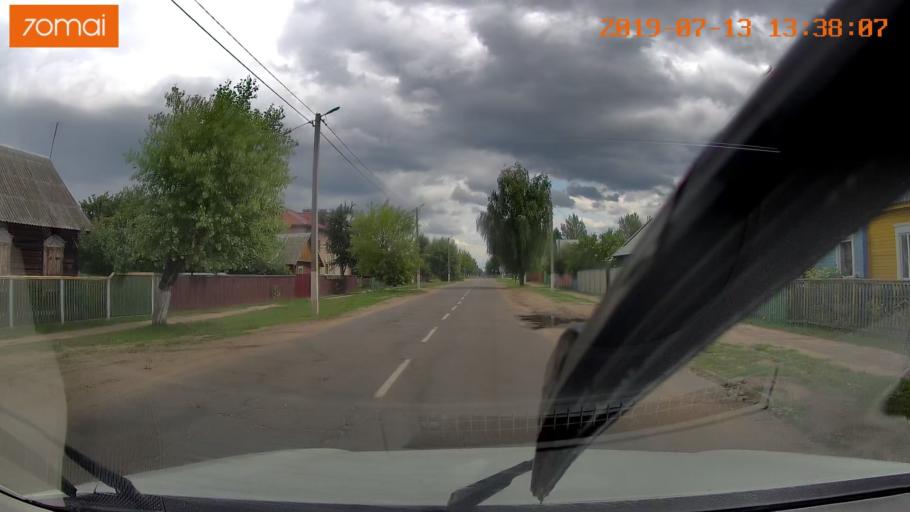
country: BY
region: Mogilev
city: Asipovichy
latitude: 53.2990
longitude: 28.6315
